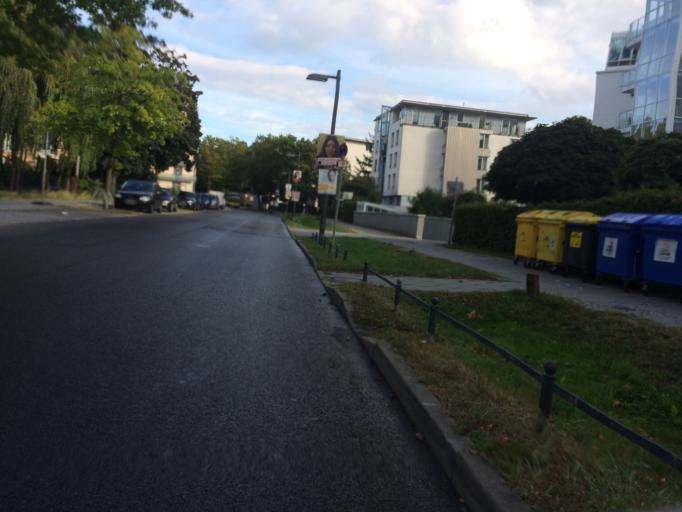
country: DE
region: Berlin
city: Treptow Bezirk
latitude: 52.4943
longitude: 13.4702
